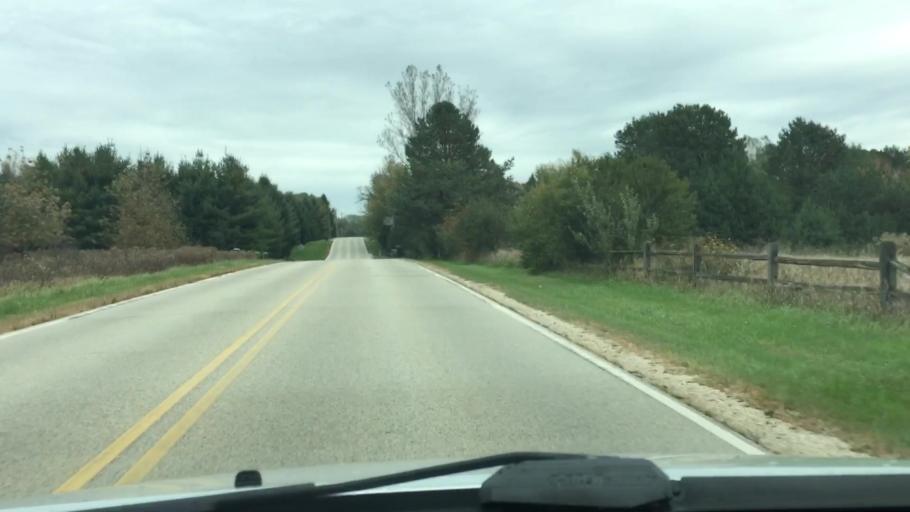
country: US
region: Wisconsin
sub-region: Waukesha County
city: Wales
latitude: 43.0112
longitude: -88.3534
